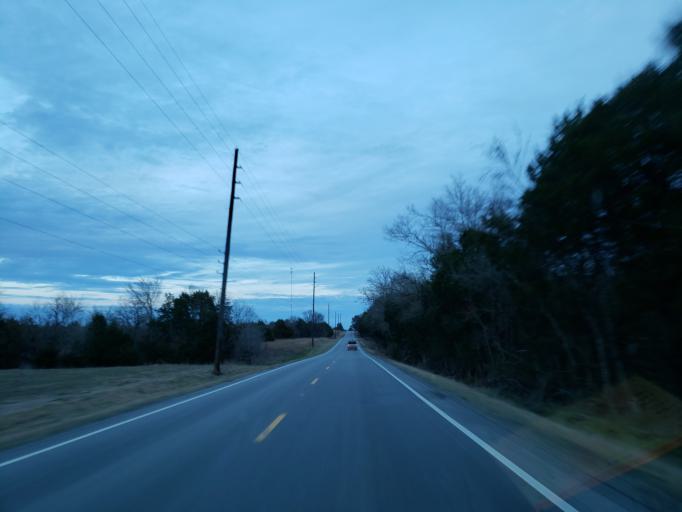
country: US
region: Alabama
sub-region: Sumter County
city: Livingston
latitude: 32.8058
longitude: -88.3028
